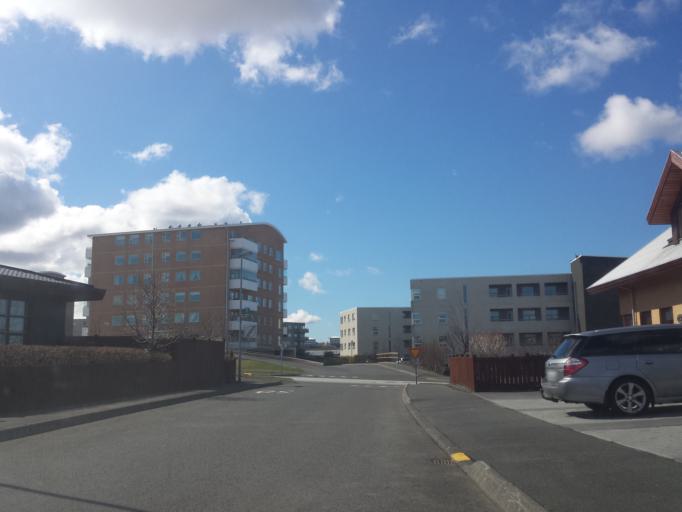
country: IS
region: Capital Region
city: Reykjavik
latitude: 64.0930
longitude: -21.8478
